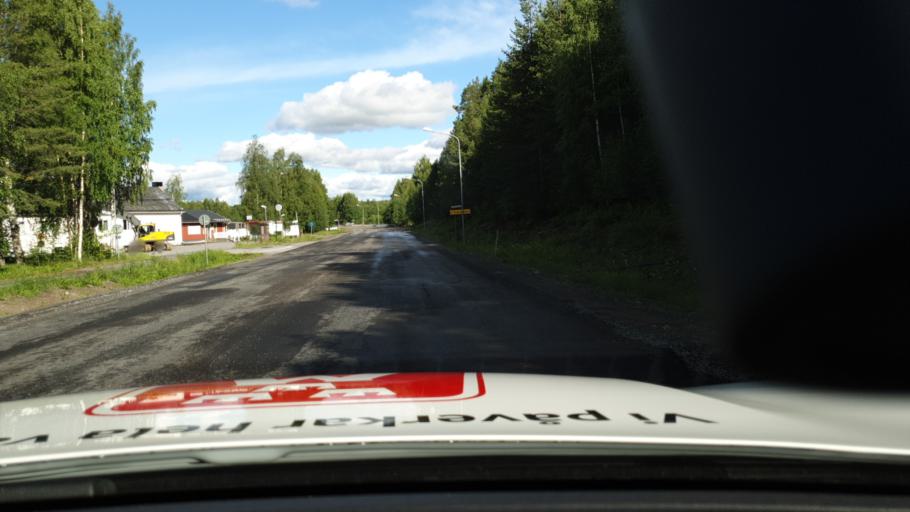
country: SE
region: Norrbotten
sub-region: Bodens Kommun
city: Boden
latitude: 65.8431
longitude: 21.6029
